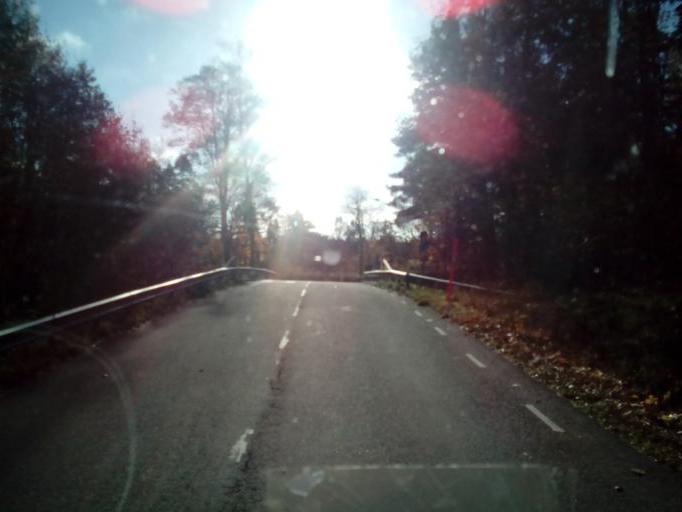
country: SE
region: Kalmar
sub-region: Vimmerby Kommun
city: Vimmerby
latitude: 57.7198
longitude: 16.0678
